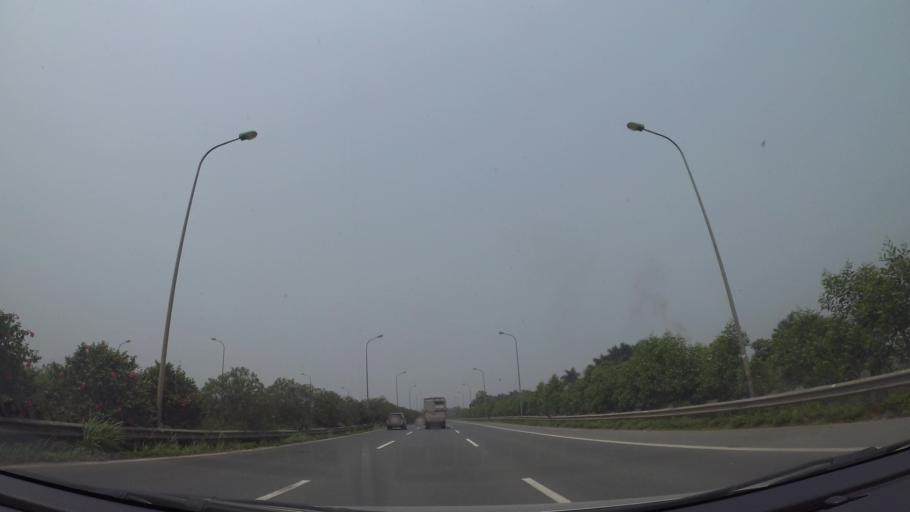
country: VN
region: Ha Noi
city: Quoc Oai
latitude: 21.0012
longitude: 105.6056
